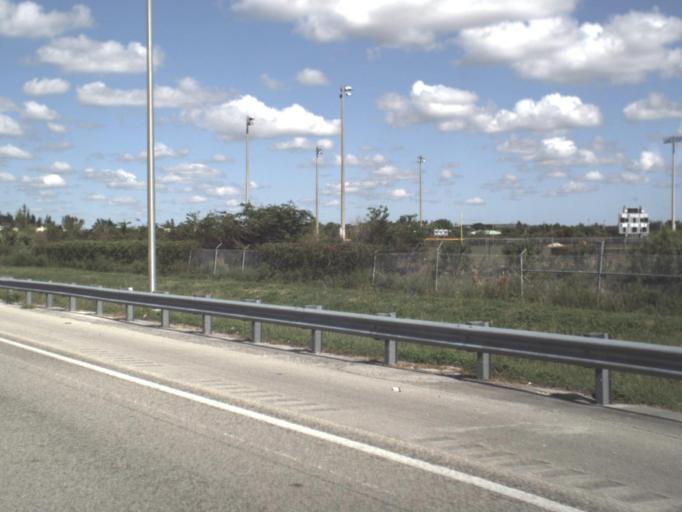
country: US
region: Florida
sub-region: Broward County
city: Coral Springs
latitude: 26.2658
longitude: -80.2969
